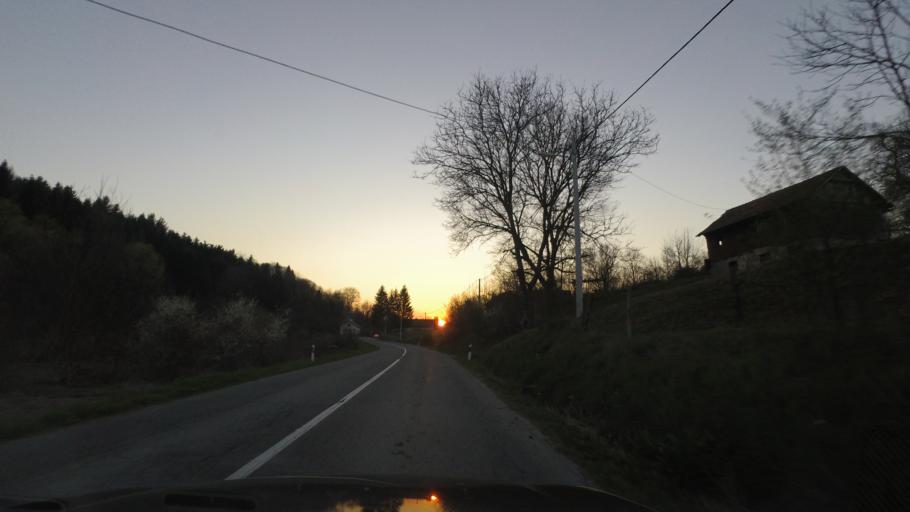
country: HR
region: Karlovacka
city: Vojnic
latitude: 45.3392
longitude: 15.7497
